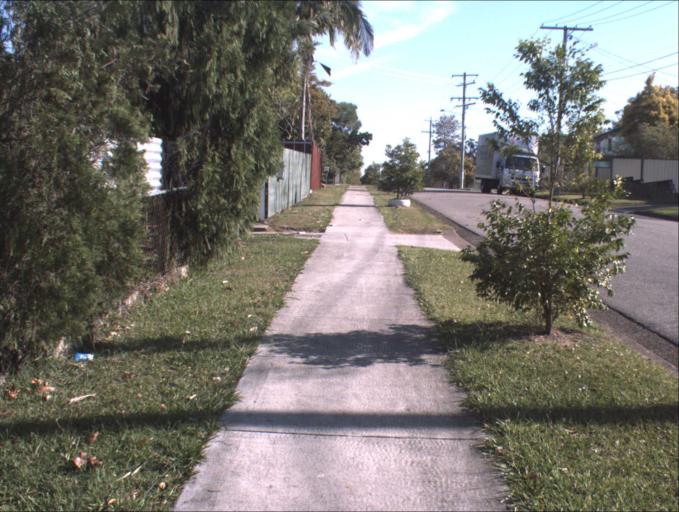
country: AU
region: Queensland
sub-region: Logan
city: Woodridge
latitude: -27.6252
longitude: 153.0975
